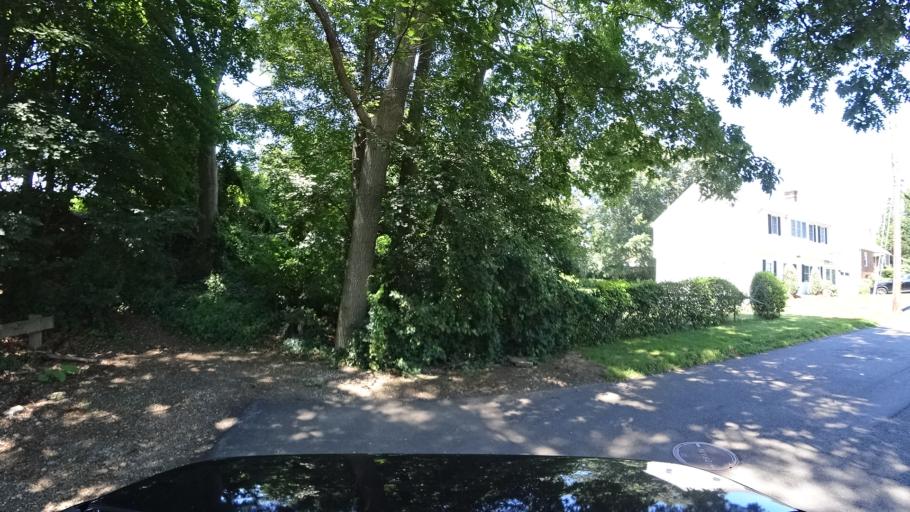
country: US
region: Massachusetts
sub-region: Norfolk County
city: Dedham
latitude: 42.2671
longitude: -71.1814
